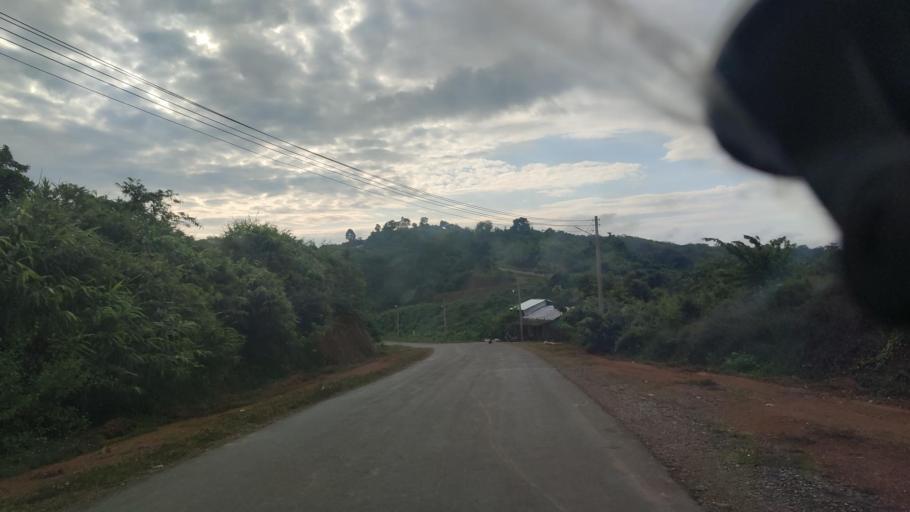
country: MM
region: Magway
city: Minbu
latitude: 19.7607
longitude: 94.0404
